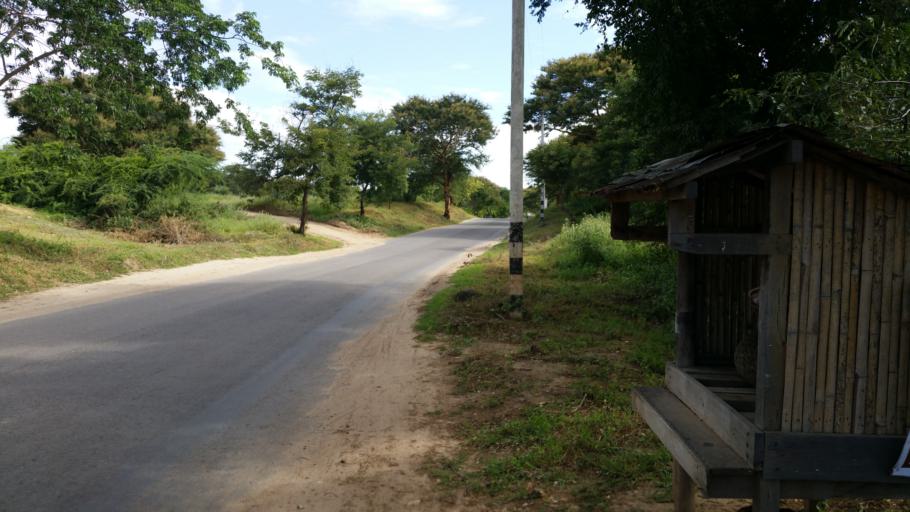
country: MM
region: Magway
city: Chauk
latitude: 21.1416
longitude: 94.8584
